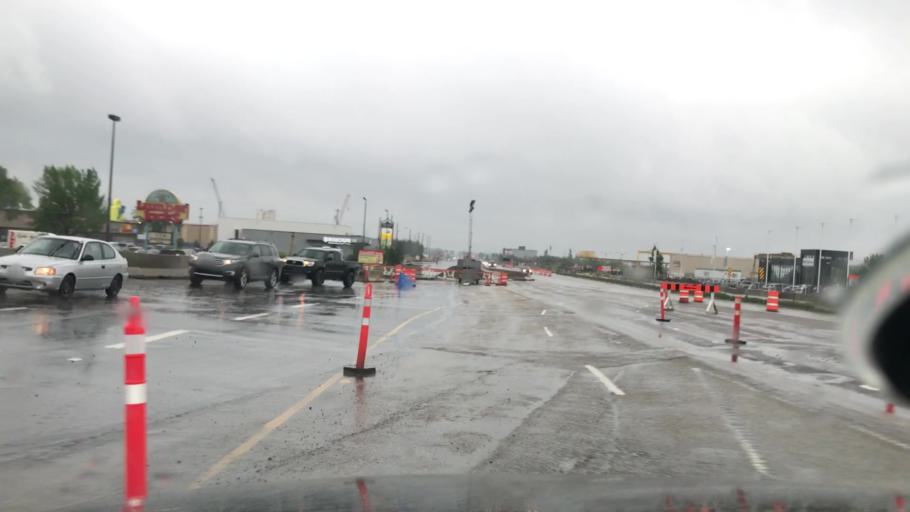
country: CA
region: Alberta
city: Edmonton
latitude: 53.4929
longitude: -113.4429
